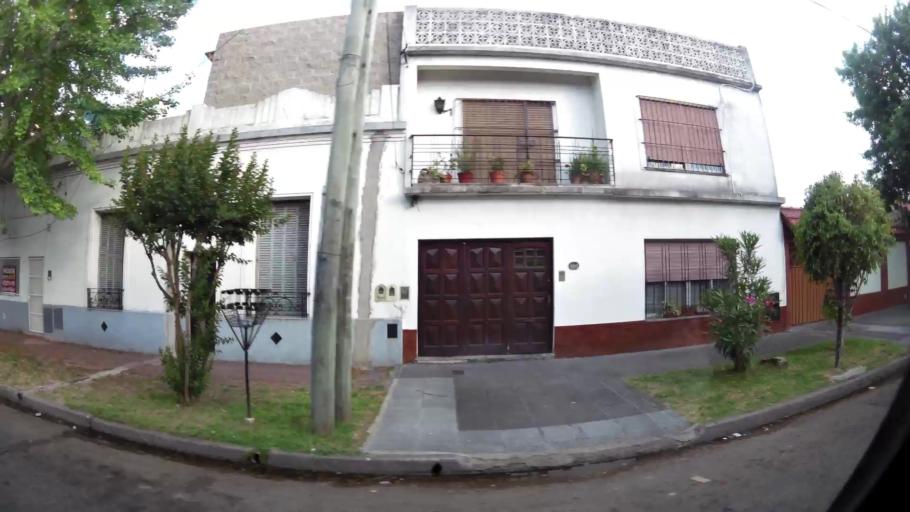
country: AR
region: Buenos Aires
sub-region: Partido de Avellaneda
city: Avellaneda
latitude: -34.6959
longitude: -58.3355
